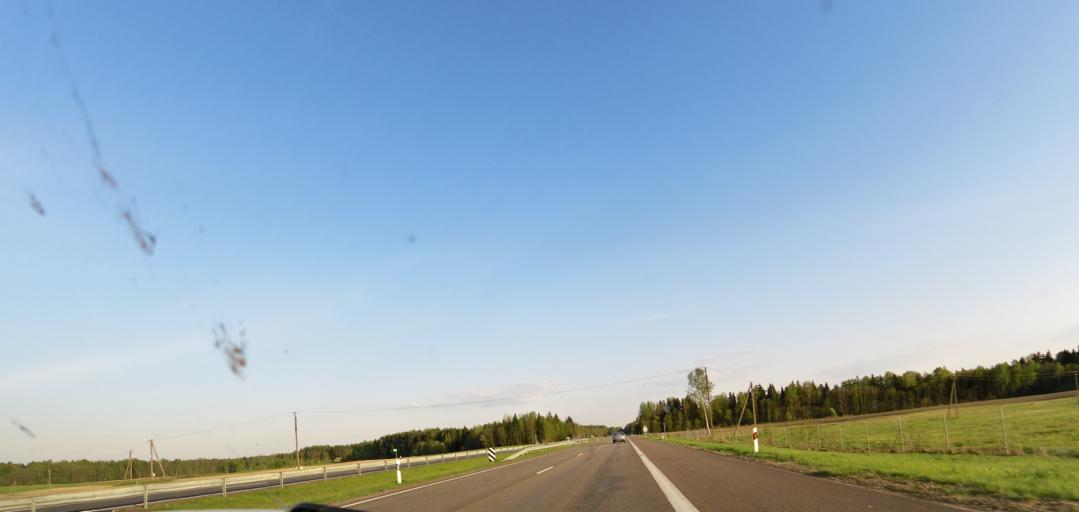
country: LT
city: Sirvintos
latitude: 55.1078
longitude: 24.8507
